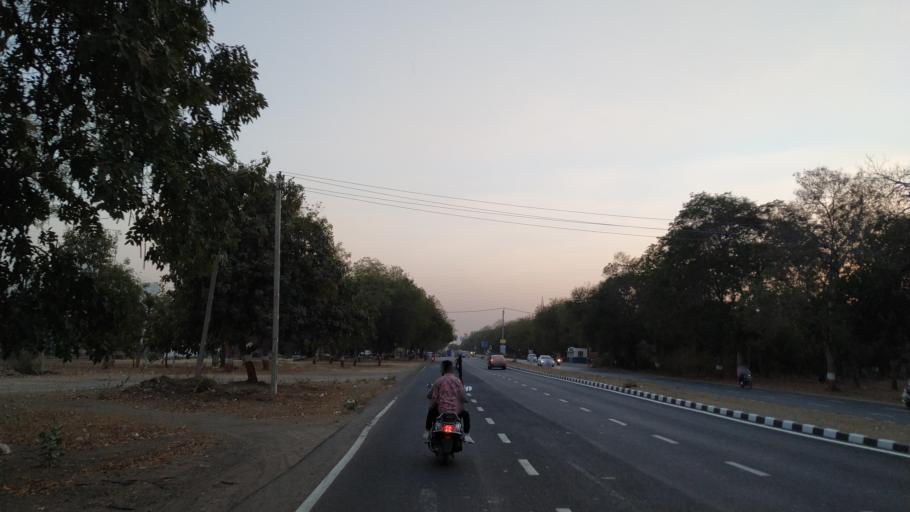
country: IN
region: Gujarat
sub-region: Gandhinagar
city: Adalaj
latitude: 23.1253
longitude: 72.6224
